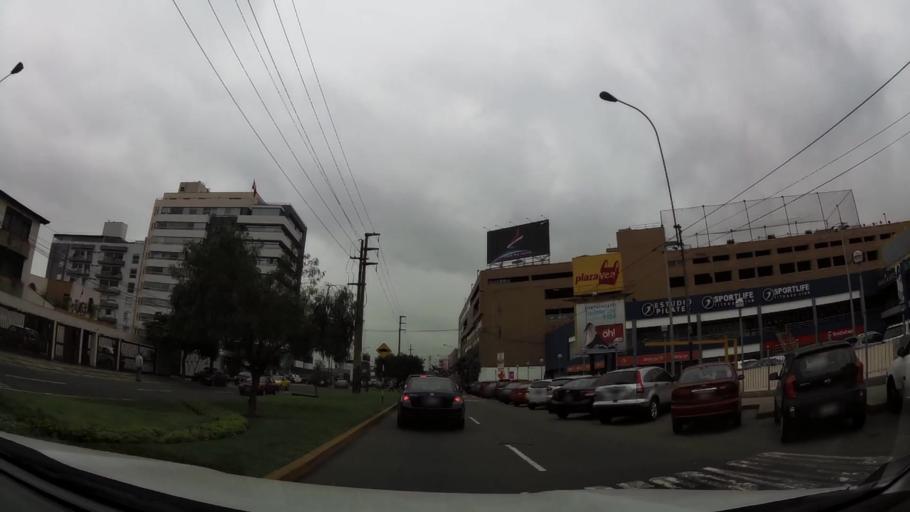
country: PE
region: Lima
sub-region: Lima
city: Surco
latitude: -12.1148
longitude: -76.9914
